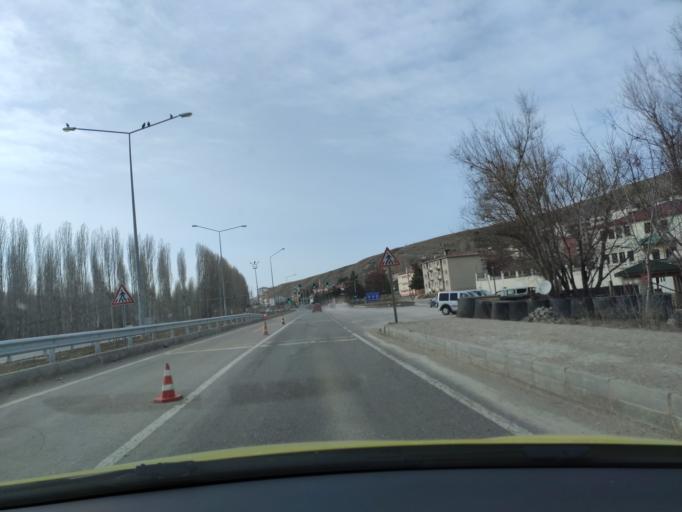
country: TR
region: Bayburt
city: Bayburt
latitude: 40.2403
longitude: 40.2479
